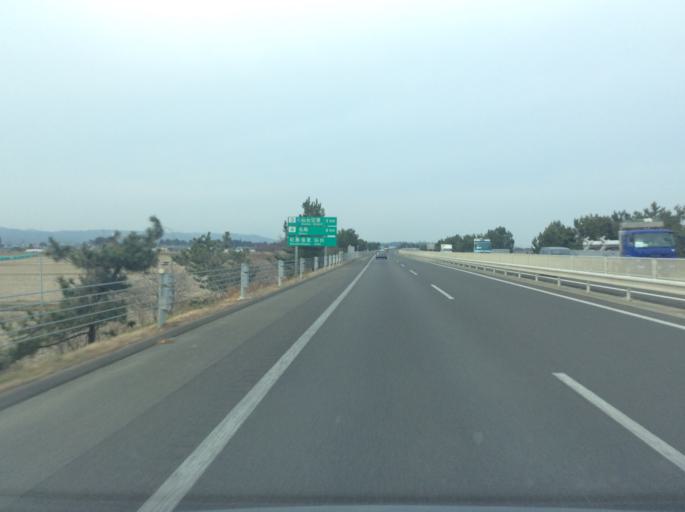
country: JP
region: Miyagi
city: Iwanuma
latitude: 38.1134
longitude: 140.8885
